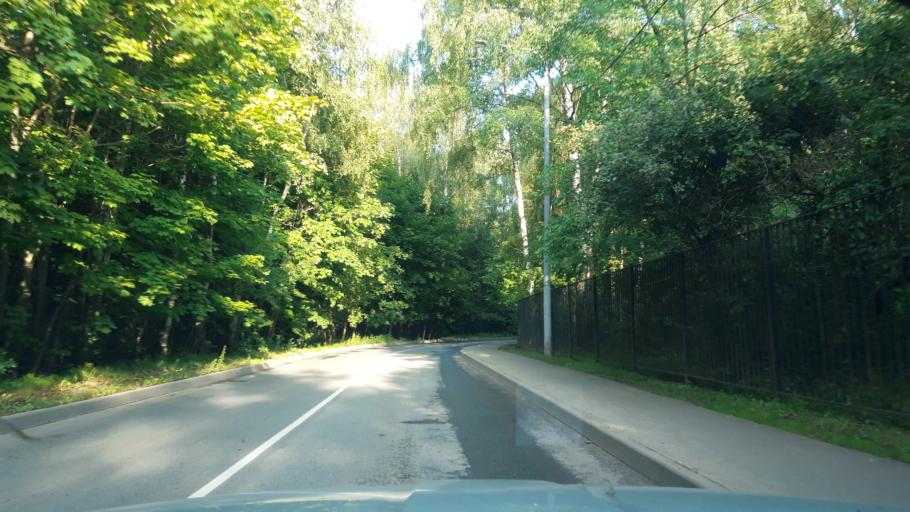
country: RU
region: Moskovskaya
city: Mendeleyevo
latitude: 56.0066
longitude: 37.2126
